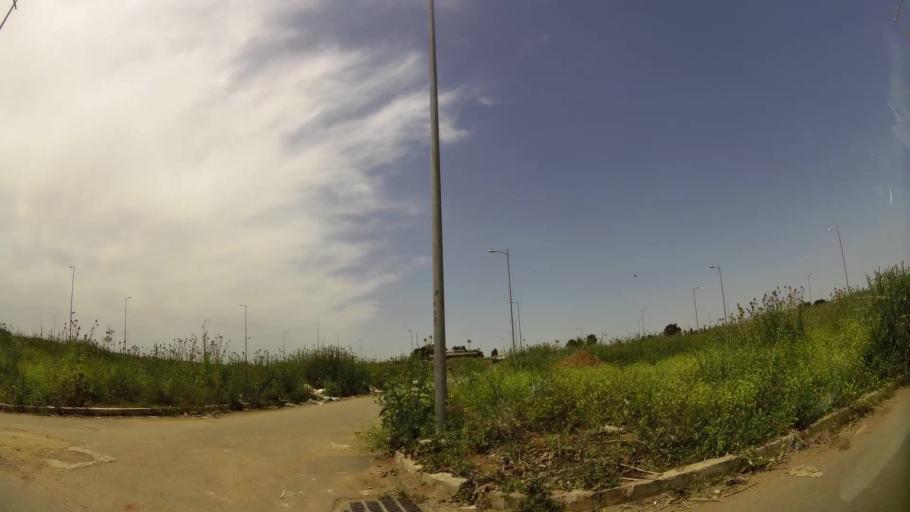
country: MA
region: Rabat-Sale-Zemmour-Zaer
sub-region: Khemisset
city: Khemisset
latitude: 33.8202
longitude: -6.0870
